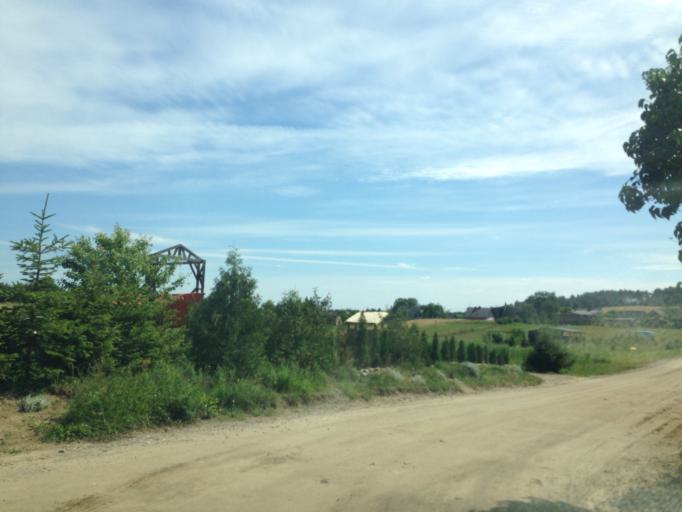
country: PL
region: Pomeranian Voivodeship
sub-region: Powiat koscierski
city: Karsin
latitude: 53.9513
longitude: 17.8717
